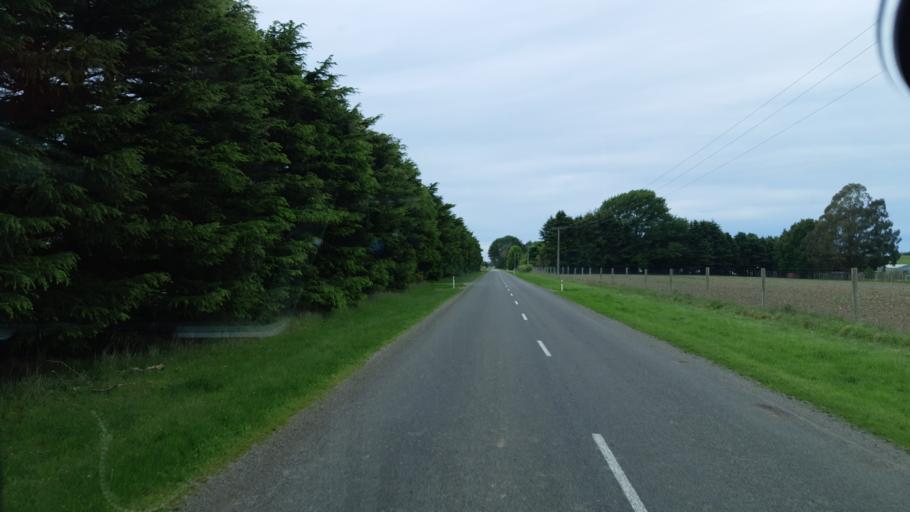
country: NZ
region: Canterbury
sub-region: Timaru District
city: Timaru
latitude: -44.4825
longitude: 171.1524
